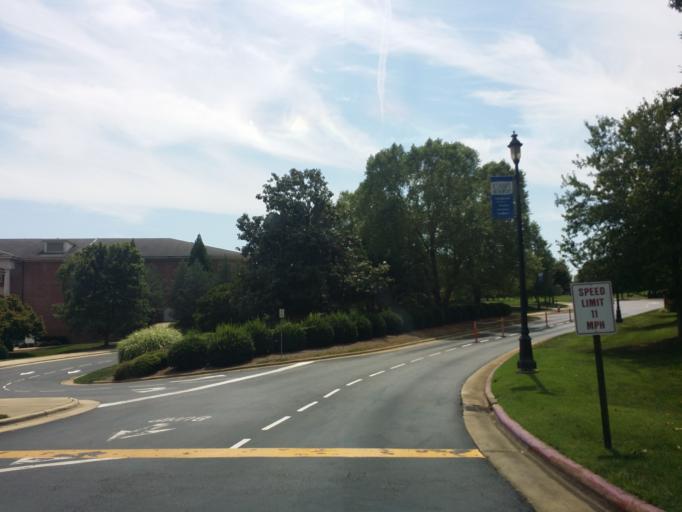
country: US
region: North Carolina
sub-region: Wake County
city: Cary
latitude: 35.8214
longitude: -78.7695
